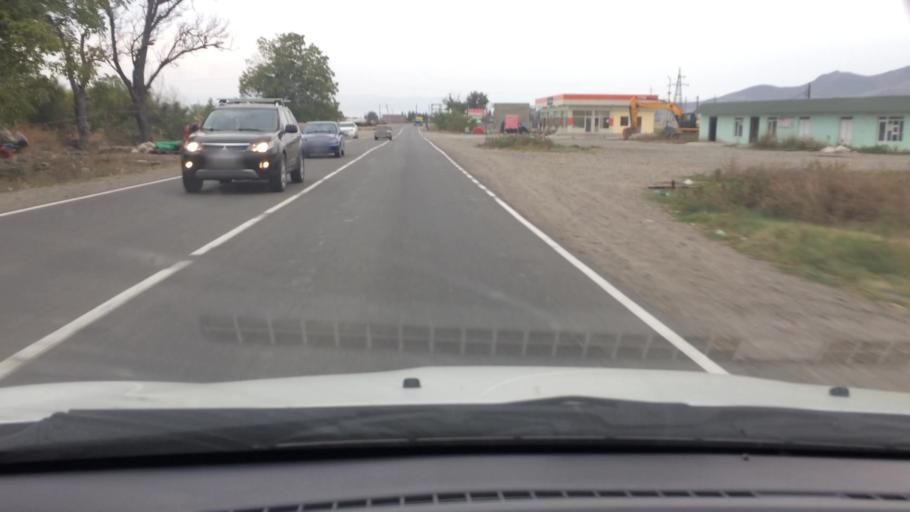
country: GE
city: Naghvarevi
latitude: 41.3964
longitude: 44.8263
